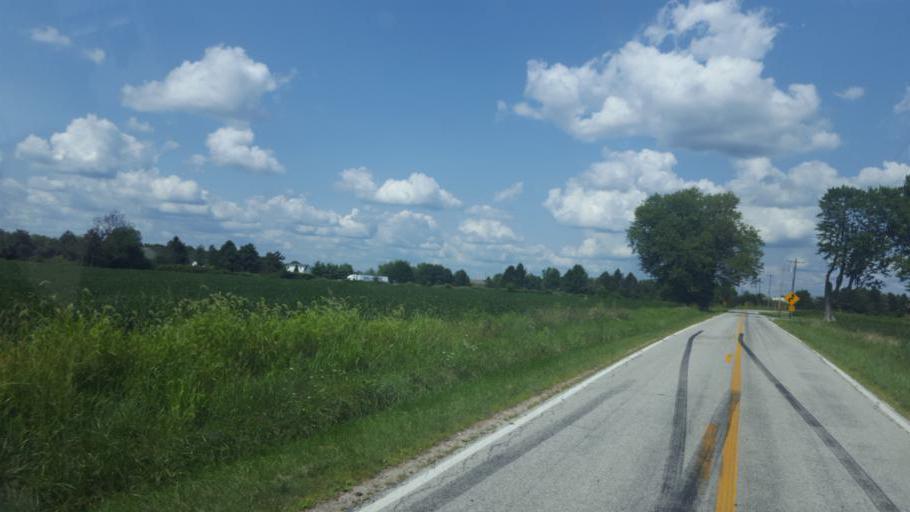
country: US
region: Ohio
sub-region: Delaware County
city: Sunbury
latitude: 40.3352
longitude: -82.8802
